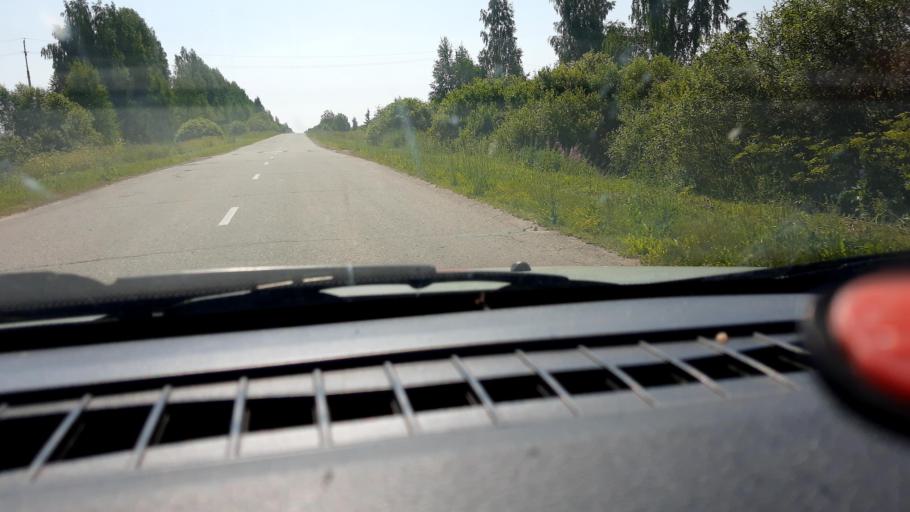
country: RU
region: Nizjnij Novgorod
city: Sharanga
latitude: 57.0444
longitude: 46.5543
